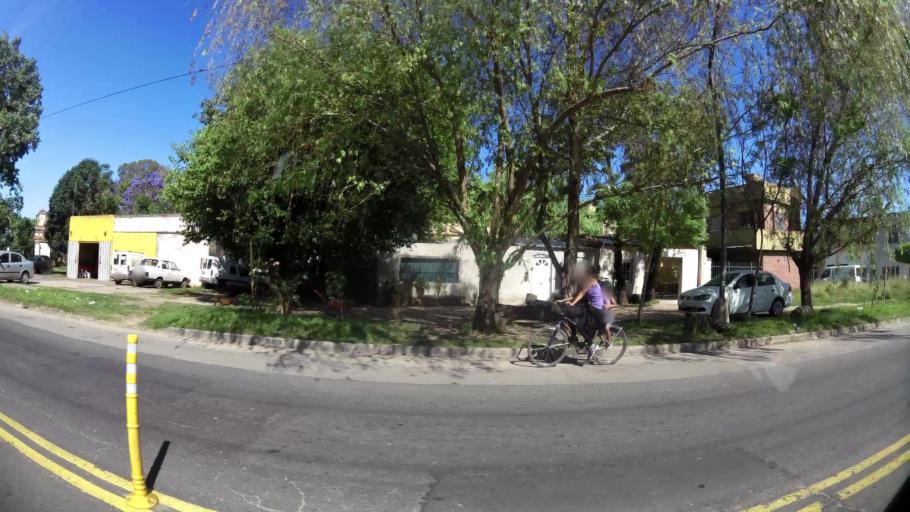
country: AR
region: Santa Fe
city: Santa Fe de la Vera Cruz
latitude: -31.6114
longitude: -60.6791
